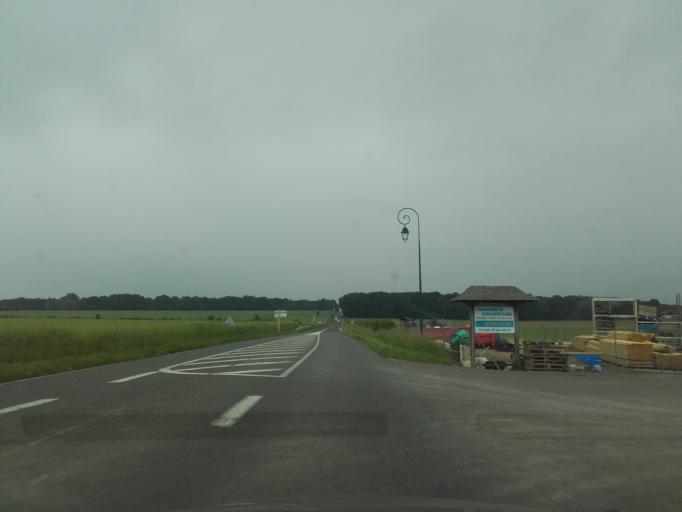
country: FR
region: Centre
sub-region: Departement d'Indre-et-Loire
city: Beaumont-la-Ronce
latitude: 47.6164
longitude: 0.6587
